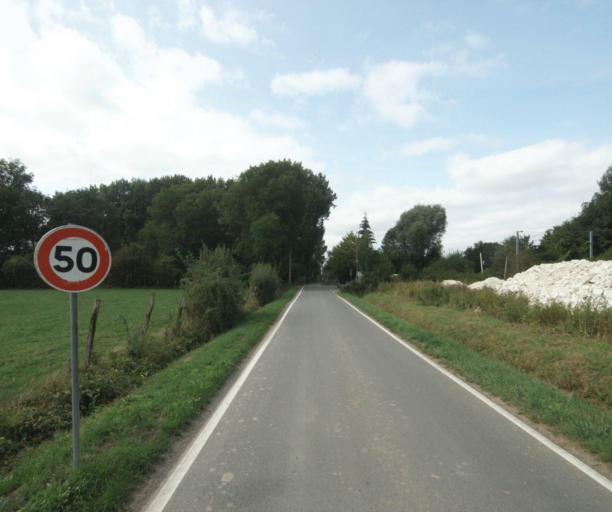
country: FR
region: Nord-Pas-de-Calais
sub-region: Departement du Nord
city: Tressin
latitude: 50.6198
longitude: 3.1982
